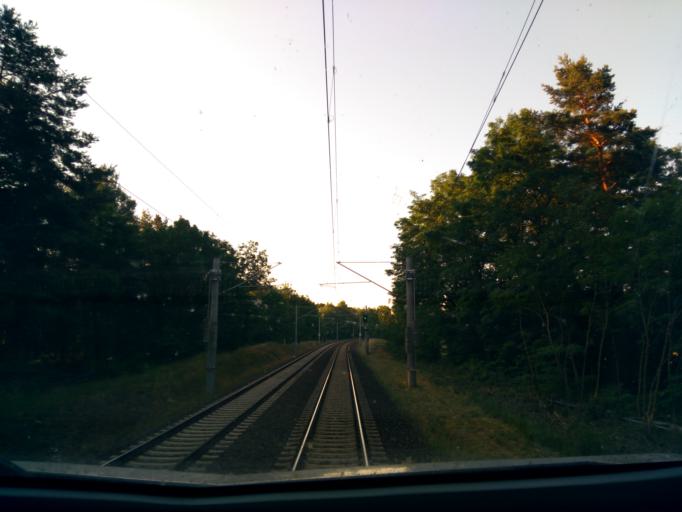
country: DE
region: Brandenburg
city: Schwerin
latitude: 52.1836
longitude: 13.6341
